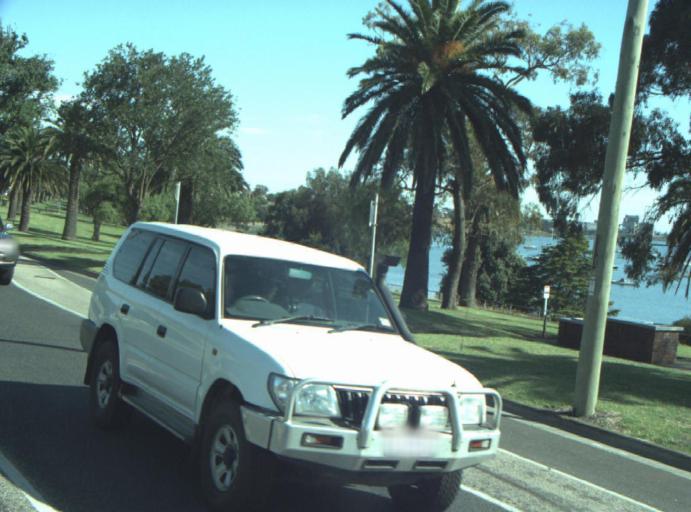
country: AU
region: Victoria
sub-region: Greater Geelong
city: Geelong
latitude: -38.1409
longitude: 144.3573
